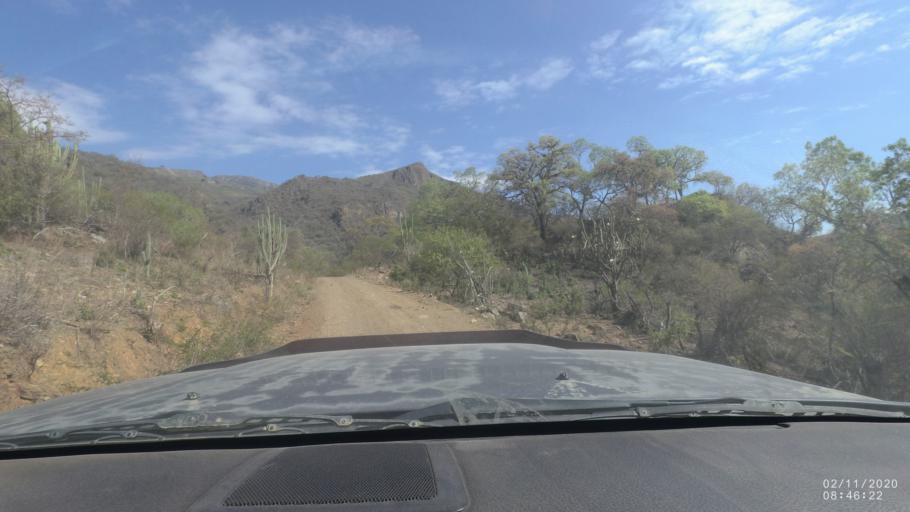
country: BO
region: Chuquisaca
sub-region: Provincia Zudanez
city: Mojocoya
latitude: -18.5646
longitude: -64.5451
